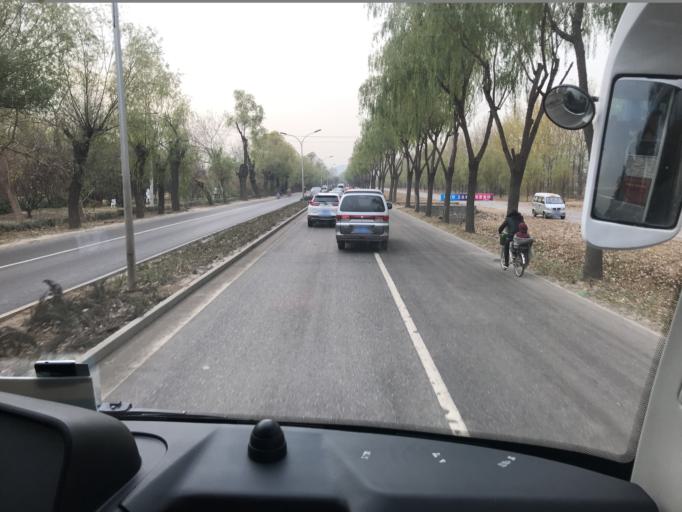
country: CN
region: Beijing
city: Wenquan
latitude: 40.0859
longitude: 116.2102
